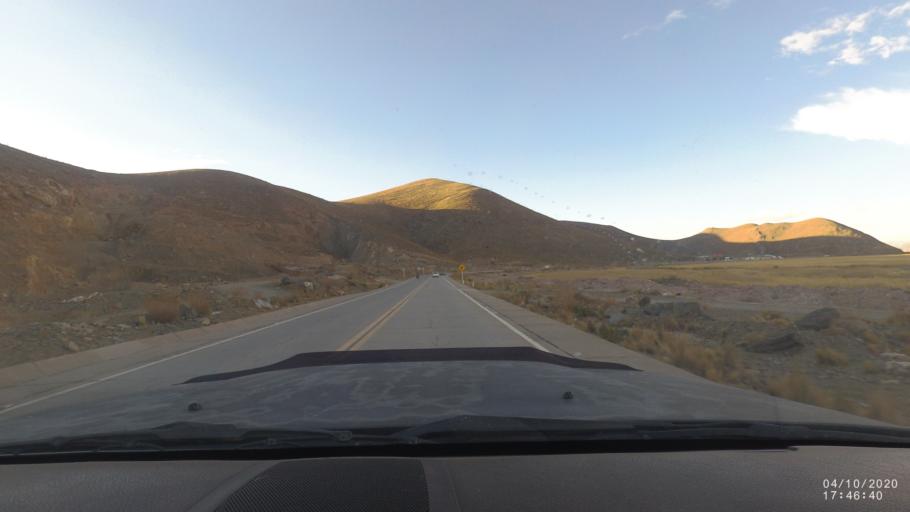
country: BO
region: Oruro
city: Oruro
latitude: -18.0299
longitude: -67.1474
